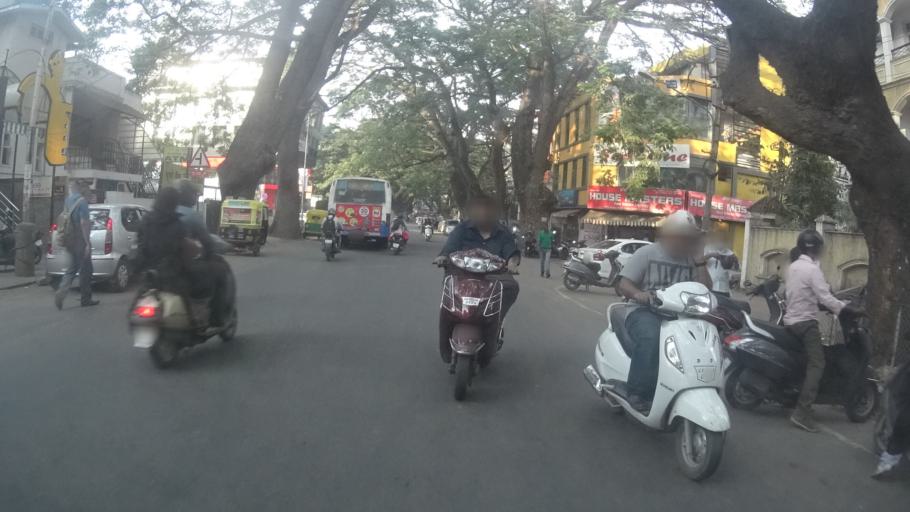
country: IN
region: Karnataka
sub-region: Bangalore Urban
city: Bangalore
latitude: 12.9974
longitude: 77.6147
